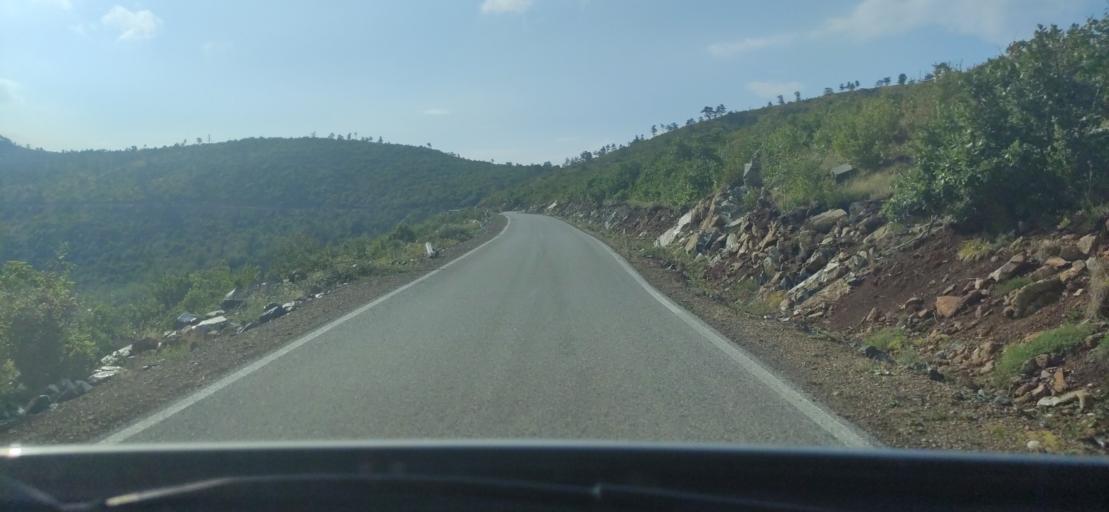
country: AL
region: Shkoder
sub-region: Rrethi i Pukes
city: Iballe
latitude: 42.1727
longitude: 20.0050
